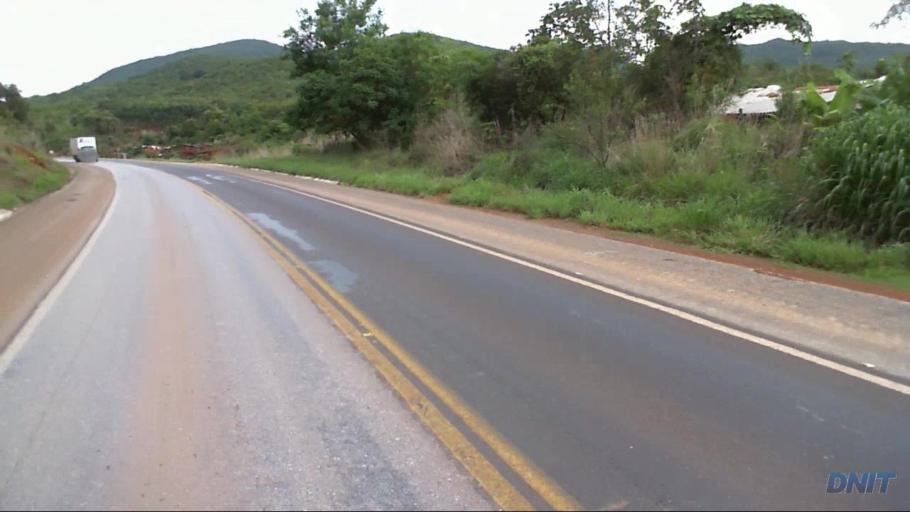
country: BR
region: Goias
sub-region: Barro Alto
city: Barro Alto
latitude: -14.9281
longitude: -48.9489
